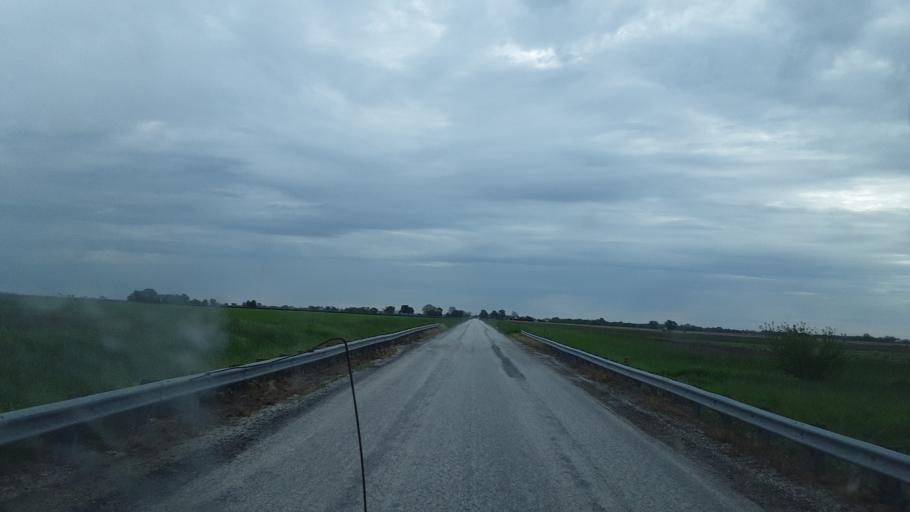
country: US
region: Illinois
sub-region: McDonough County
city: Macomb
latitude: 40.3819
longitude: -90.6729
